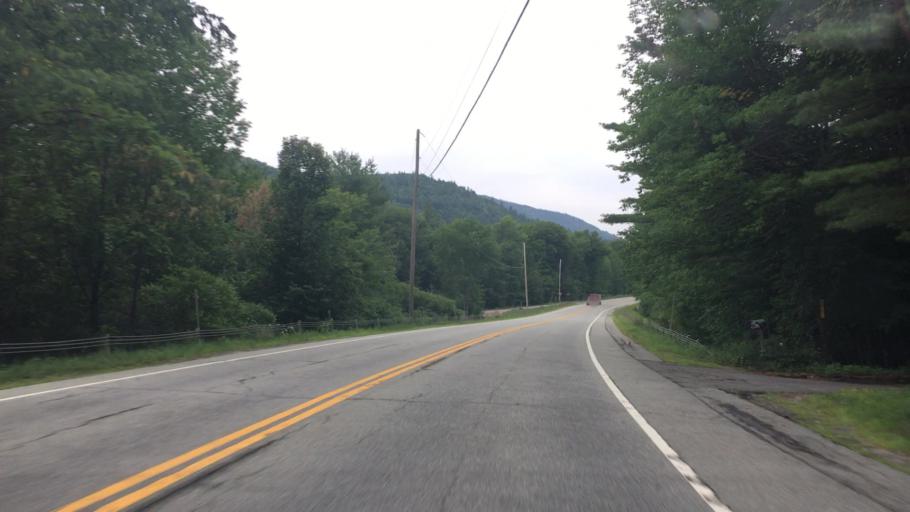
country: US
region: New York
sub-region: Essex County
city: Lake Placid
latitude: 44.3140
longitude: -73.7854
